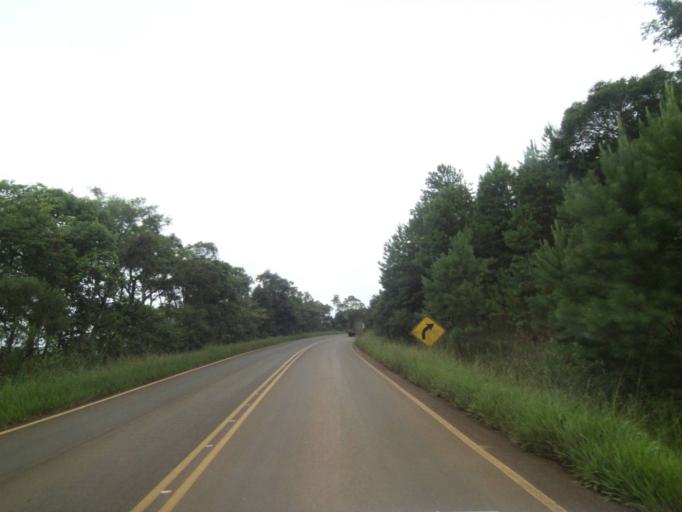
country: BR
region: Parana
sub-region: Pitanga
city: Pitanga
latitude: -24.9187
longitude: -51.8704
